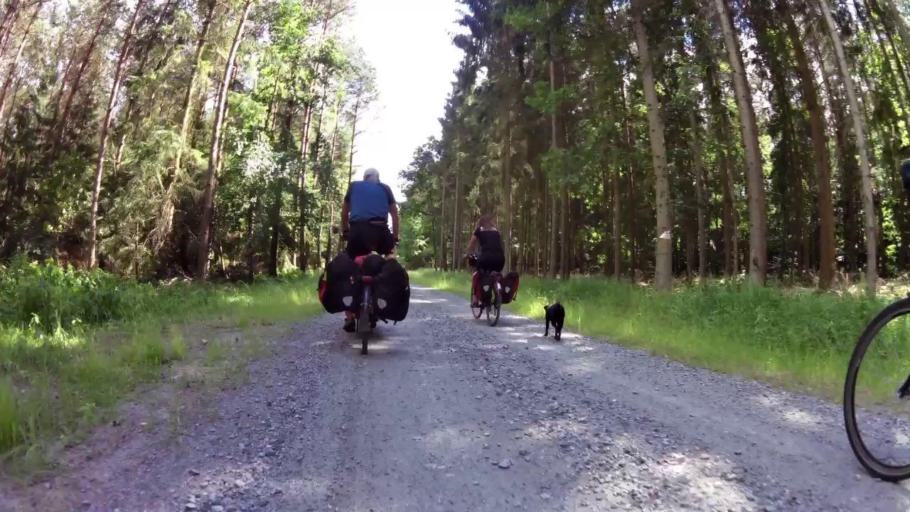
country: PL
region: West Pomeranian Voivodeship
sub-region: Powiat lobeski
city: Lobez
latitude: 53.6775
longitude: 15.5524
